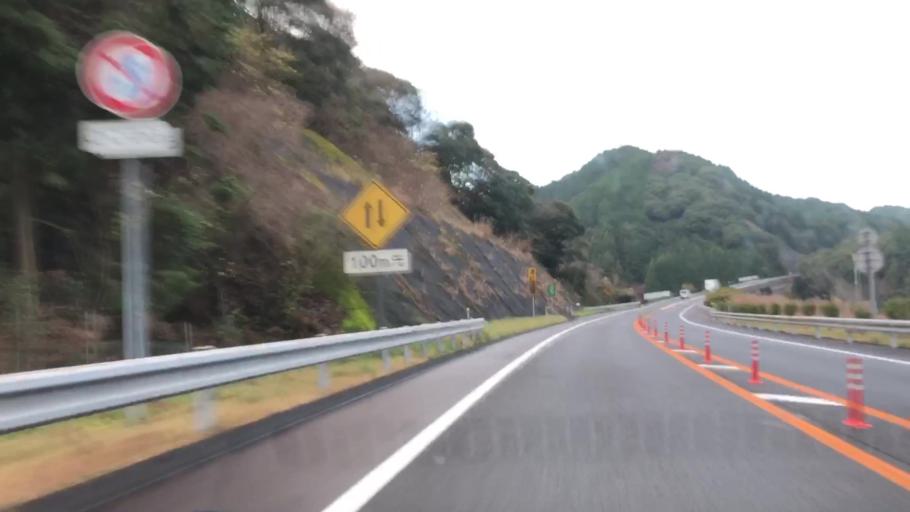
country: JP
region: Saga Prefecture
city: Ureshinomachi-shimojuku
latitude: 33.1437
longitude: 129.9784
